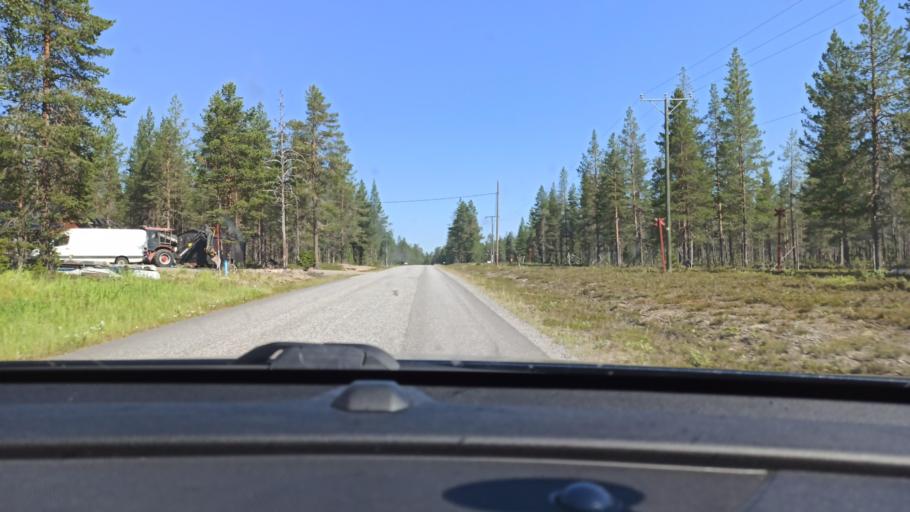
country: FI
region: Lapland
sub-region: Tunturi-Lappi
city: Kolari
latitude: 67.6538
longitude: 24.1633
